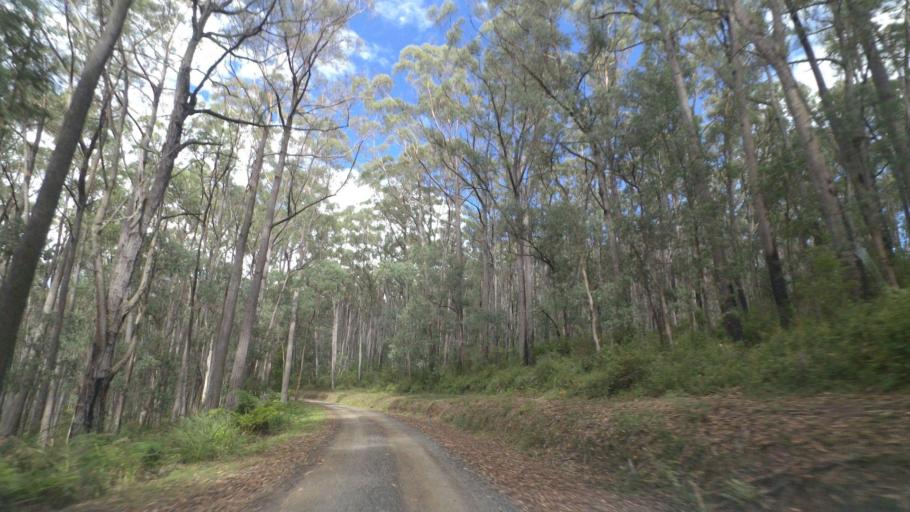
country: AU
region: Victoria
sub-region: Cardinia
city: Gembrook
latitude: -37.9098
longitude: 145.6219
